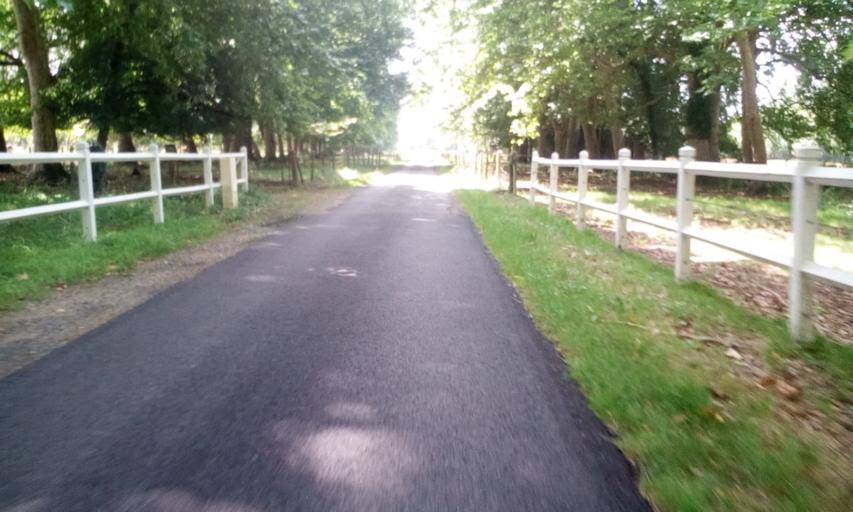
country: FR
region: Lower Normandy
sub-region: Departement du Calvados
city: Bellengreville
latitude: 49.1390
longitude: -0.2214
